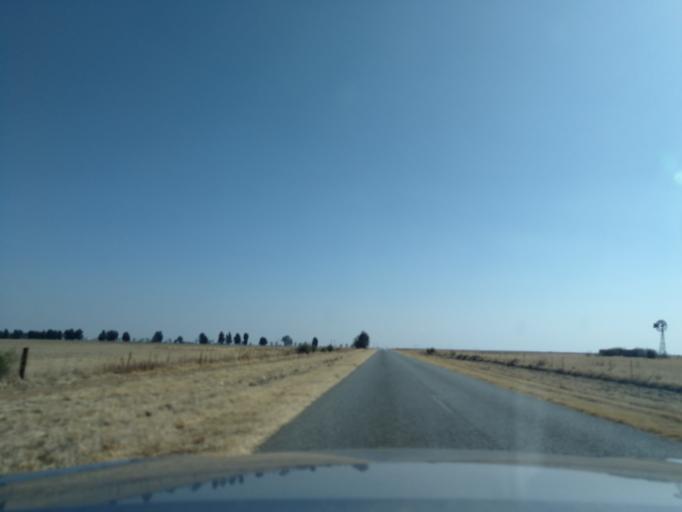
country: ZA
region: North-West
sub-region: Dr Kenneth Kaunda District Municipality
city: Orkney
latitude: -27.0644
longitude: 26.8324
